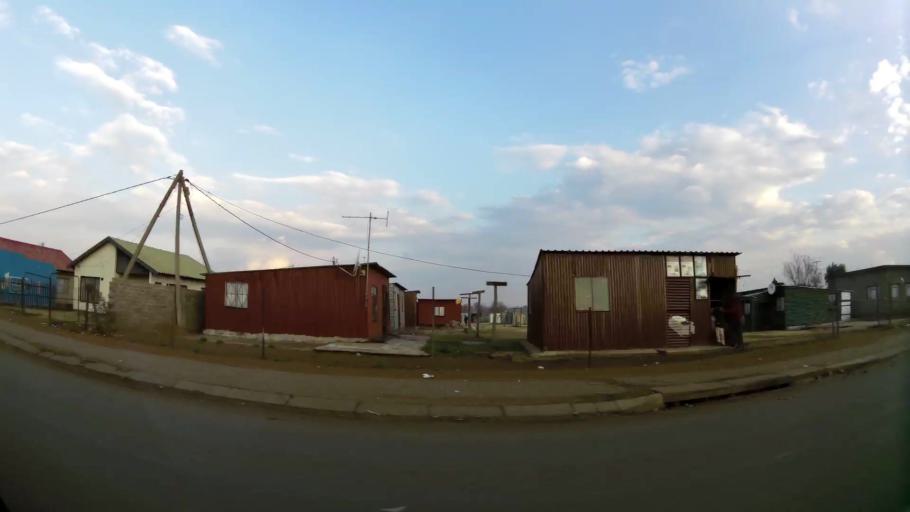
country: ZA
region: Gauteng
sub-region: City of Johannesburg Metropolitan Municipality
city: Orange Farm
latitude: -26.5358
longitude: 27.8404
